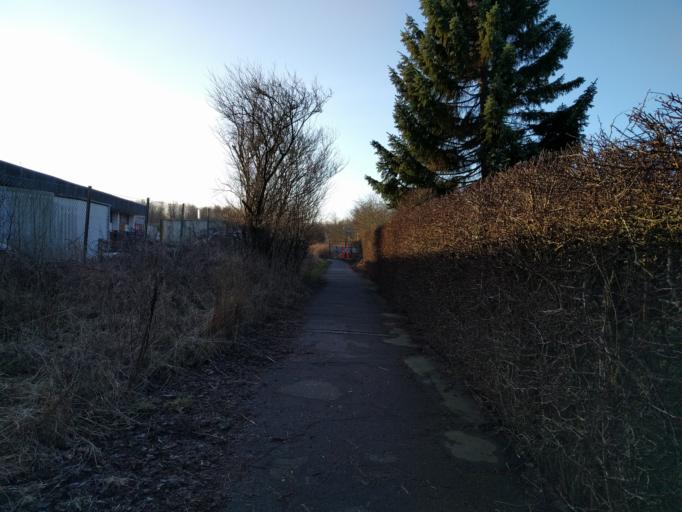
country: DK
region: North Denmark
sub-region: Alborg Kommune
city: Aalborg
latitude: 57.0259
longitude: 9.9124
